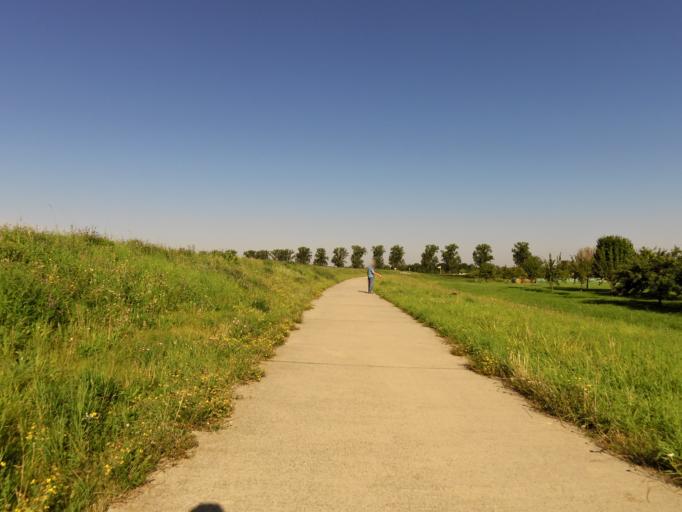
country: DE
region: Hesse
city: Biebesheim
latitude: 49.7726
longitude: 8.4601
